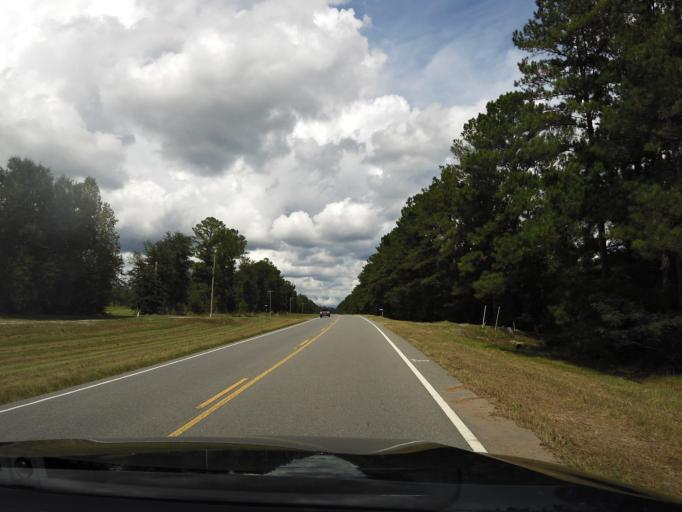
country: US
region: Georgia
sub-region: Brantley County
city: Nahunta
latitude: 31.1025
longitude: -82.0048
